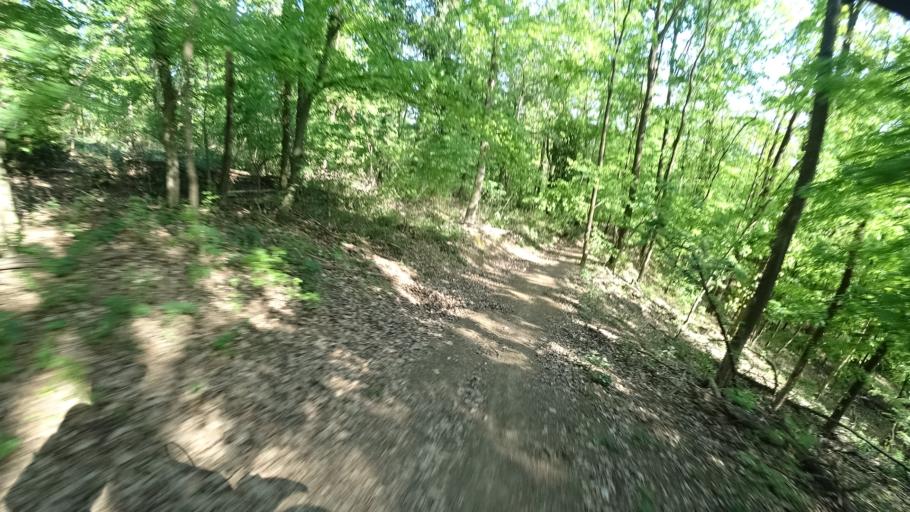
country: HR
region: Grad Zagreb
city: Stenjevec
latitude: 45.8461
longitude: 15.9169
